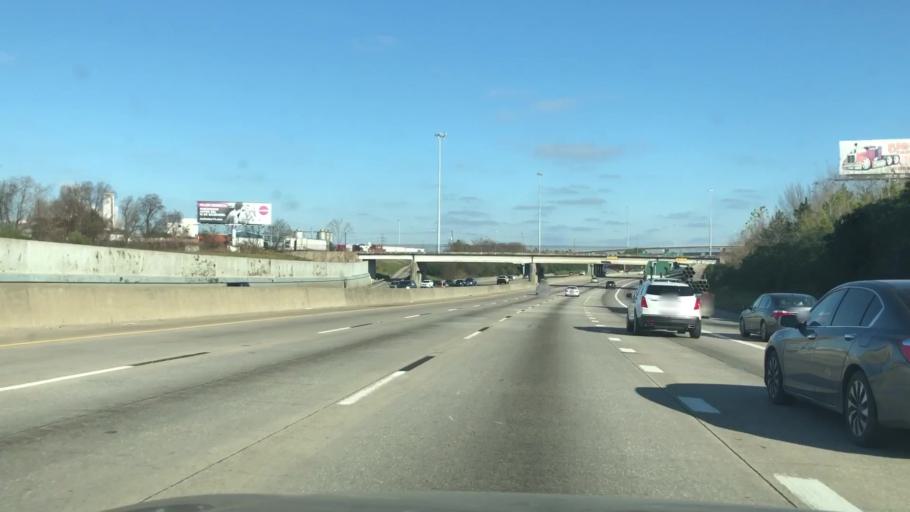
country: US
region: Texas
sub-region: Harris County
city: Jacinto City
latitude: 29.7667
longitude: -95.2653
